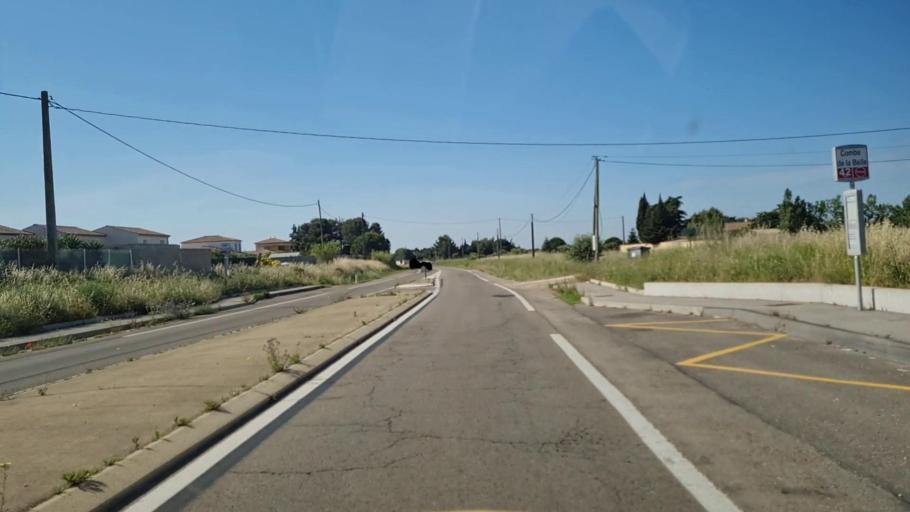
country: FR
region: Languedoc-Roussillon
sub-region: Departement du Gard
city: Saint-Gilles
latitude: 43.6977
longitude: 4.4249
